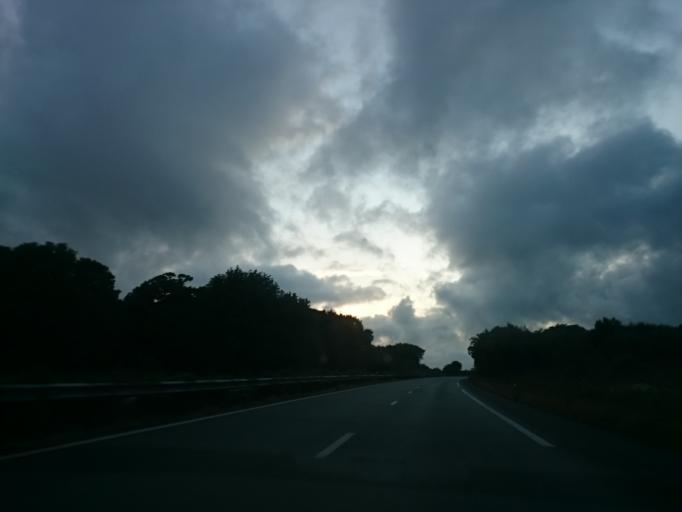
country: FR
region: Brittany
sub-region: Departement du Finistere
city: Concarneau
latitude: 47.9233
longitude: -3.8922
